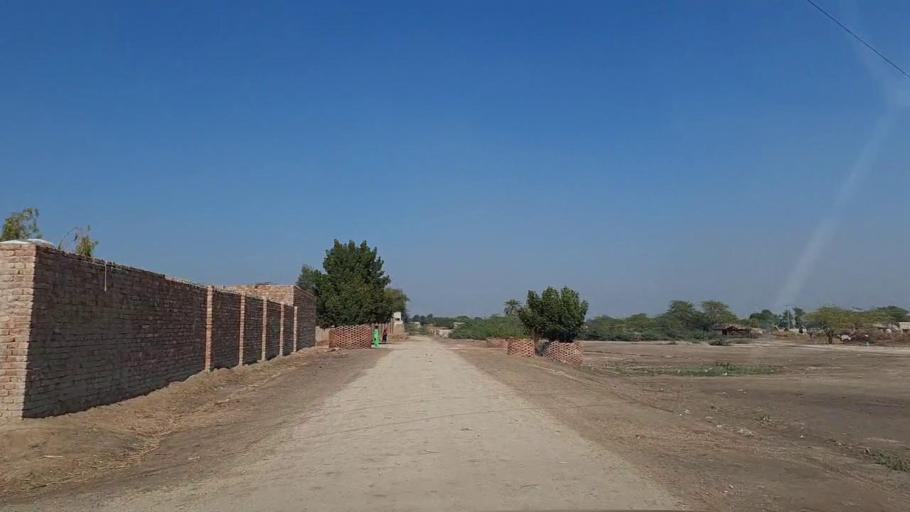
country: PK
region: Sindh
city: Nawabshah
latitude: 26.3383
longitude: 68.3545
